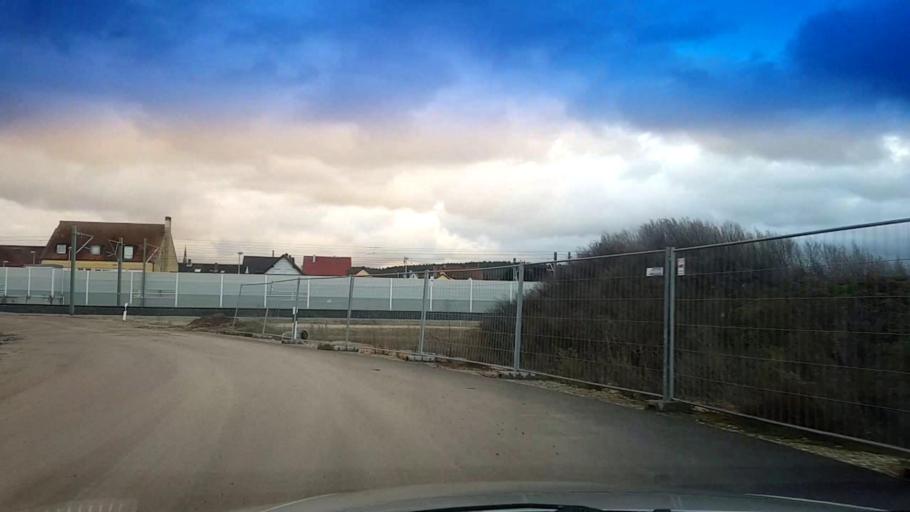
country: DE
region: Bavaria
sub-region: Upper Franconia
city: Zapfendorf
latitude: 50.0178
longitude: 10.9280
